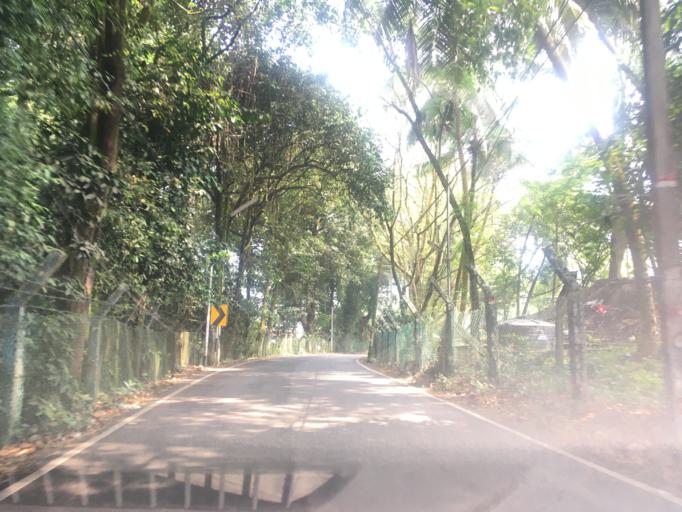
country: IN
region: Kerala
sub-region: Ernakulam
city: Elur
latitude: 10.0461
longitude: 76.3072
